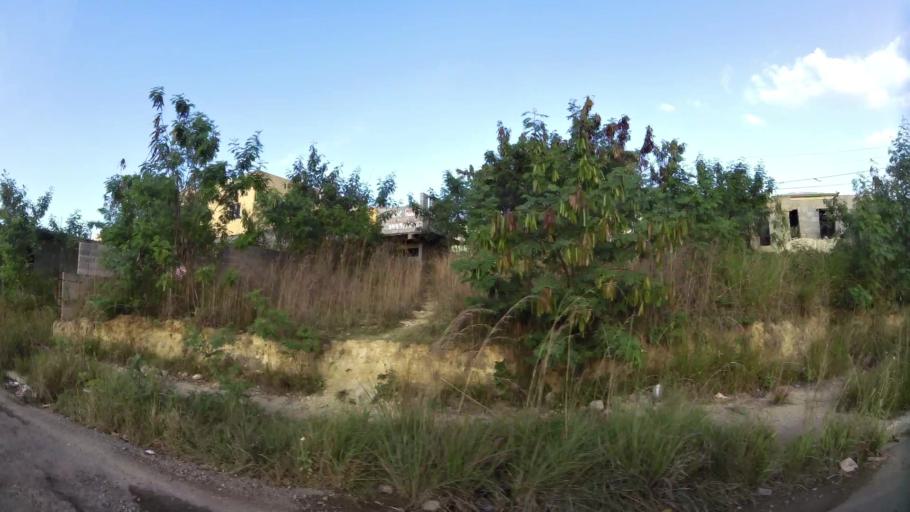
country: DO
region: Nacional
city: La Agustina
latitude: 18.5444
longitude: -69.9223
